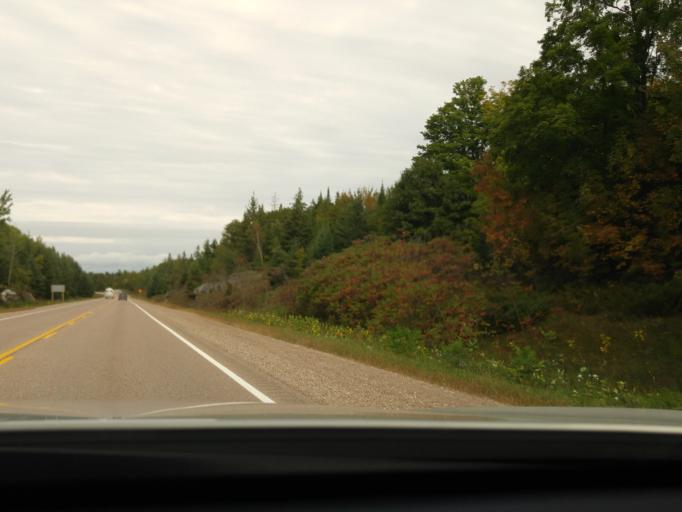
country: CA
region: Ontario
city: Renfrew
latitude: 45.5472
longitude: -76.7296
